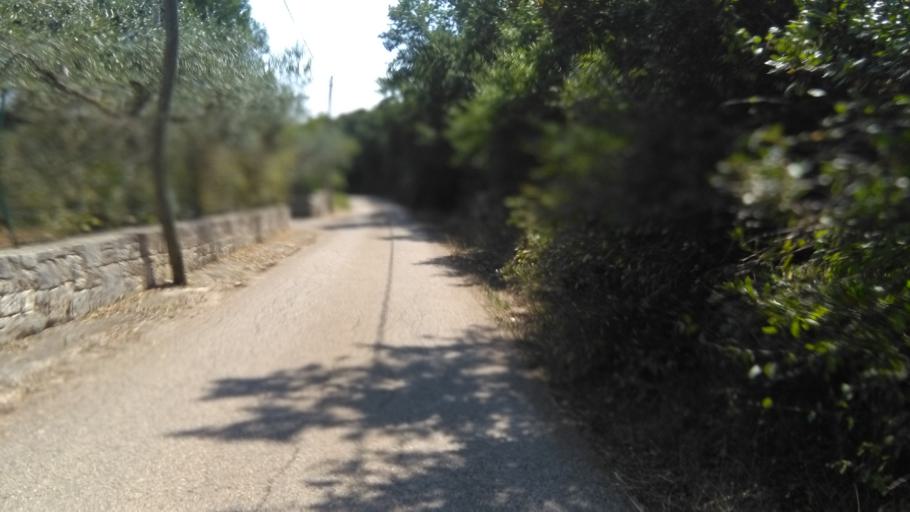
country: IT
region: Apulia
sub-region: Provincia di Bari
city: Noci
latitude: 40.8167
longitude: 17.1548
